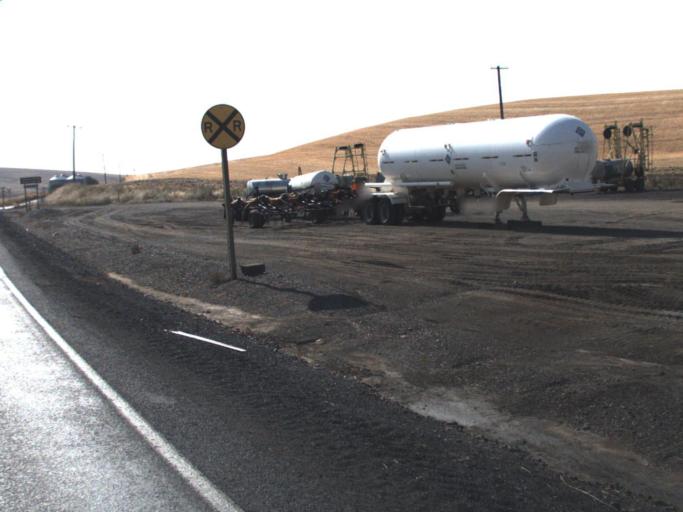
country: US
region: Washington
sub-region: Whitman County
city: Colfax
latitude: 47.1231
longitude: -117.2325
